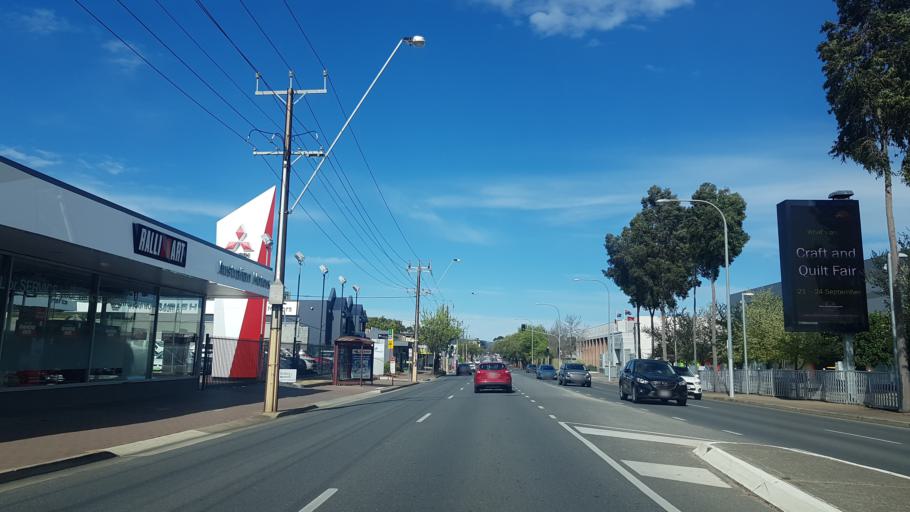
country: AU
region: South Australia
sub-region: Unley
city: Wayville
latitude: -34.9442
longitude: 138.5891
